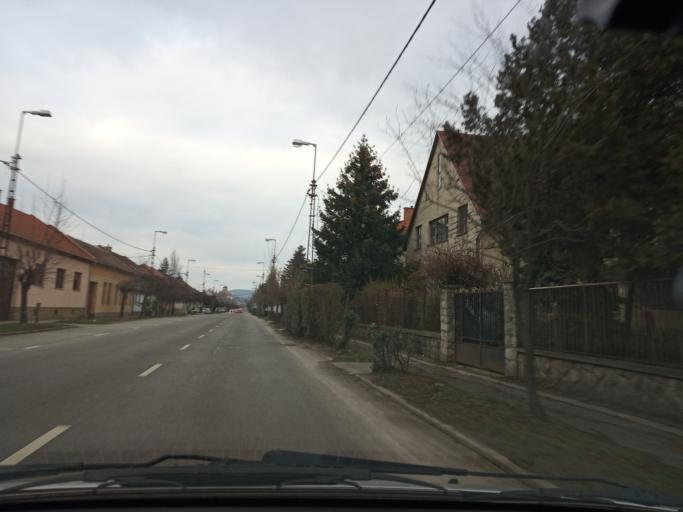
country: HU
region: Komarom-Esztergom
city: Esztergom
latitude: 47.7772
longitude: 18.7389
